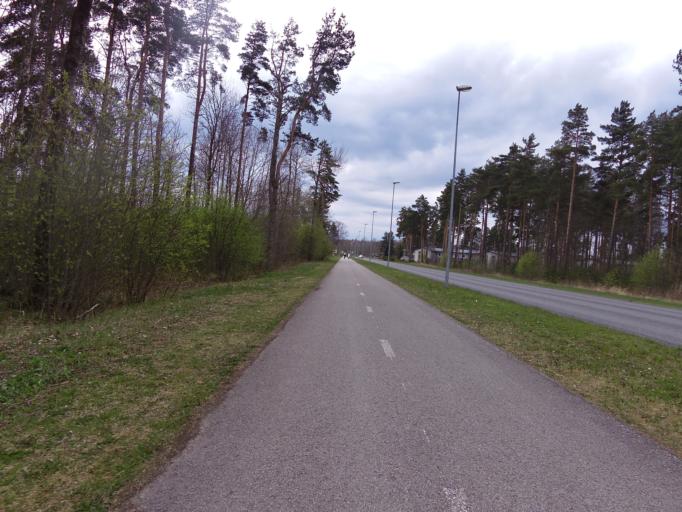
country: EE
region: Harju
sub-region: Kiili vald
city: Kiili
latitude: 59.3609
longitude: 24.8144
